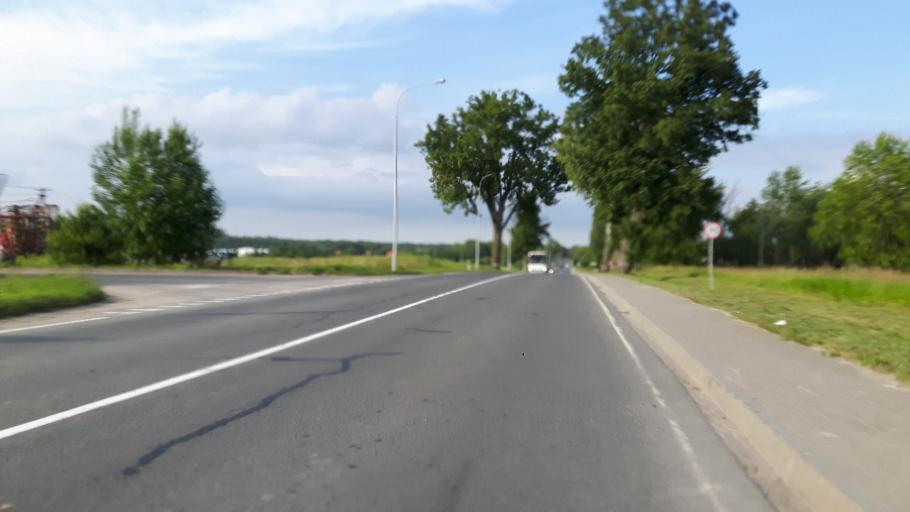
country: RU
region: Kaliningrad
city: Ladushkin
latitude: 54.5485
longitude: 20.1484
